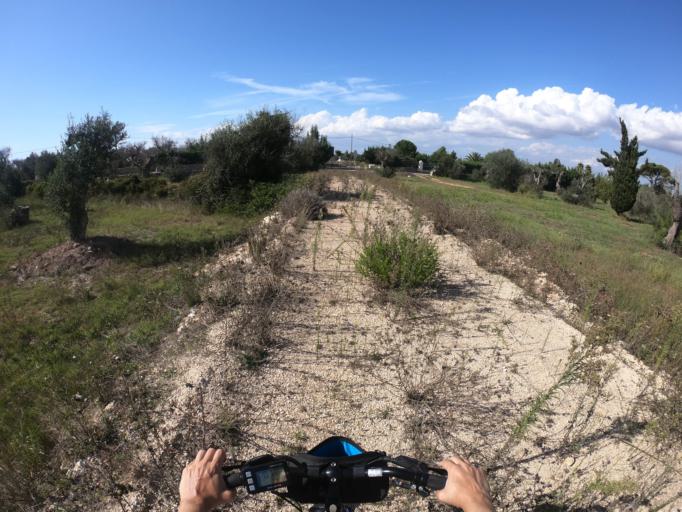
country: IT
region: Apulia
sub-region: Provincia di Lecce
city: Galatone
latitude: 40.1420
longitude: 18.0529
